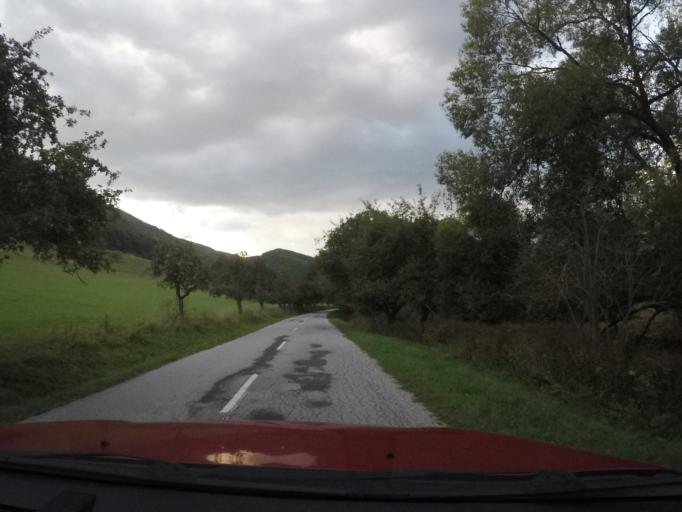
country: SK
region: Kosicky
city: Medzev
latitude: 48.6284
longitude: 20.7466
